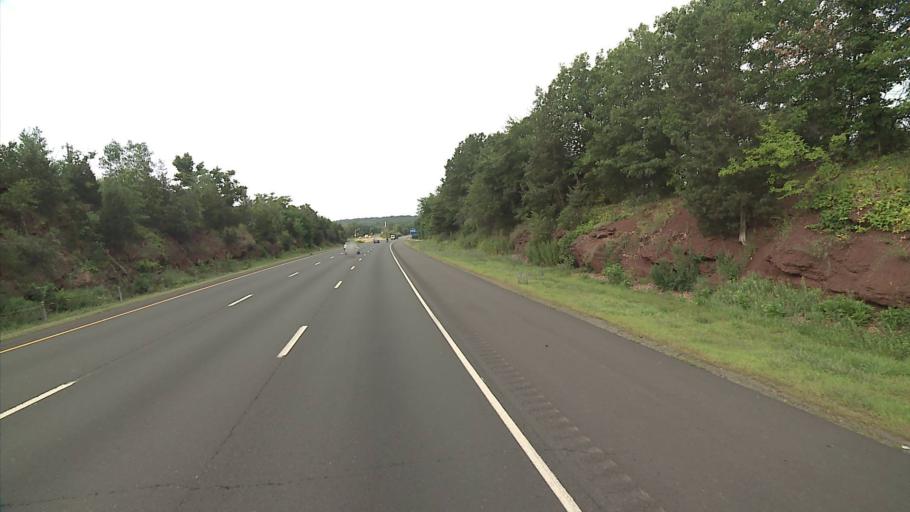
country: US
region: Connecticut
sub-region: Hartford County
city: Plainville
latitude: 41.6366
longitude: -72.8687
